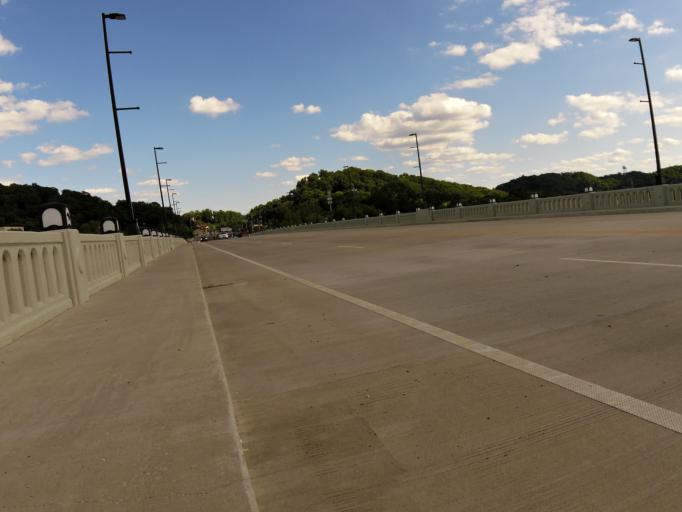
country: US
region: Tennessee
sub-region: Knox County
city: Knoxville
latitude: 35.9568
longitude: -83.9181
